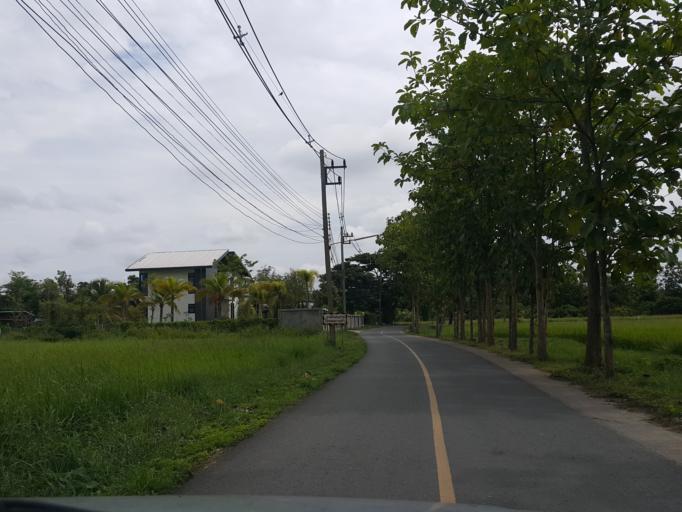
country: TH
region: Chiang Mai
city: San Sai
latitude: 18.8430
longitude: 99.1440
